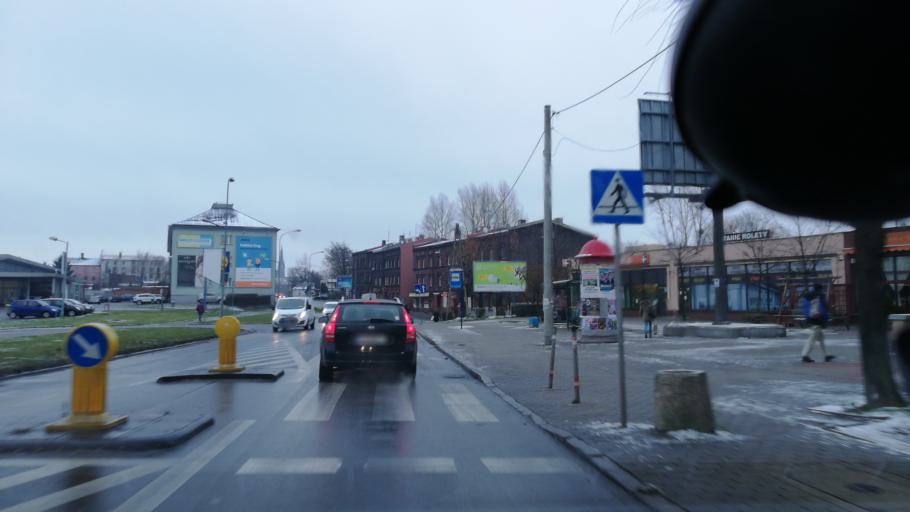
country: PL
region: Silesian Voivodeship
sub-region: Chorzow
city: Chorzow
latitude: 50.2978
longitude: 18.9688
